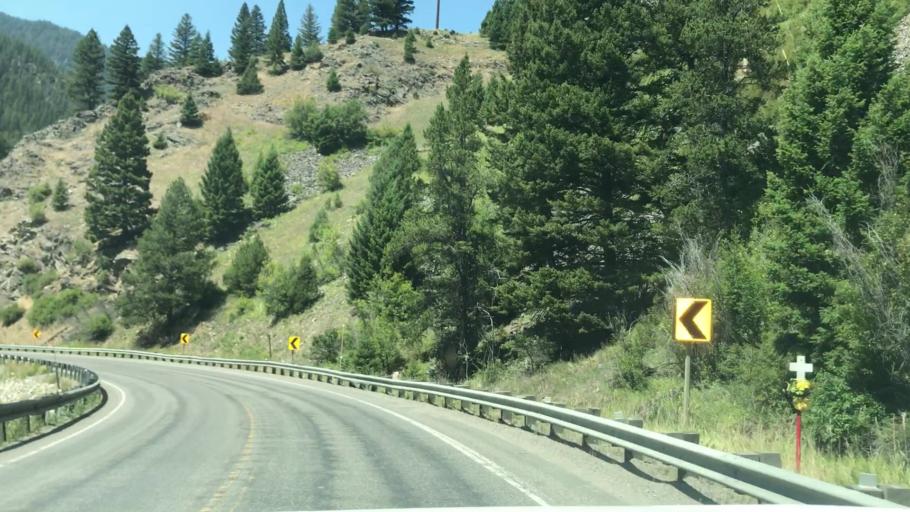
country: US
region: Montana
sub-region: Gallatin County
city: Big Sky
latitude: 45.4073
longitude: -111.2215
